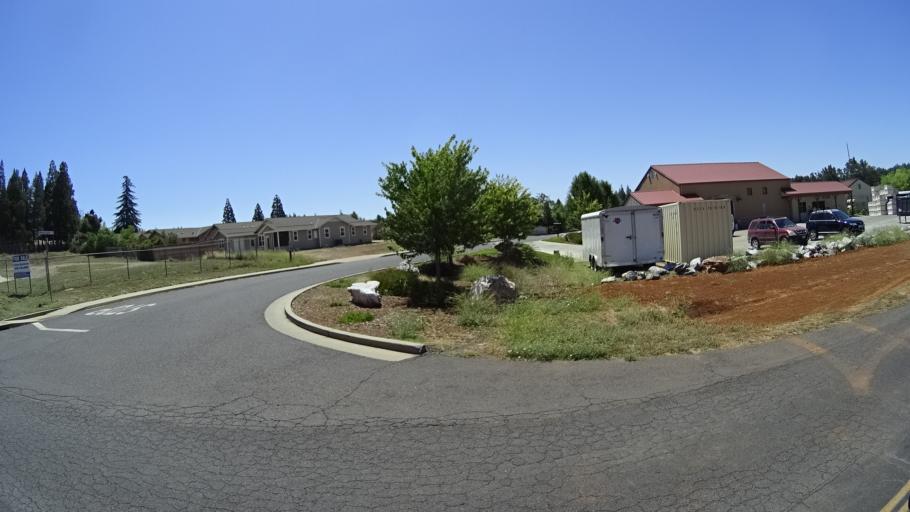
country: US
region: California
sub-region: Calaveras County
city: Murphys
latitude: 38.1420
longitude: -120.4595
